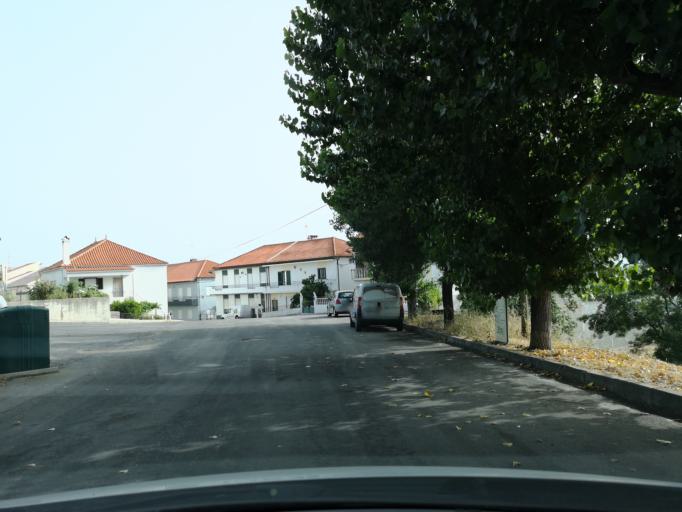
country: PT
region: Castelo Branco
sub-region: Belmonte
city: Belmonte
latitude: 40.3523
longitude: -7.3533
